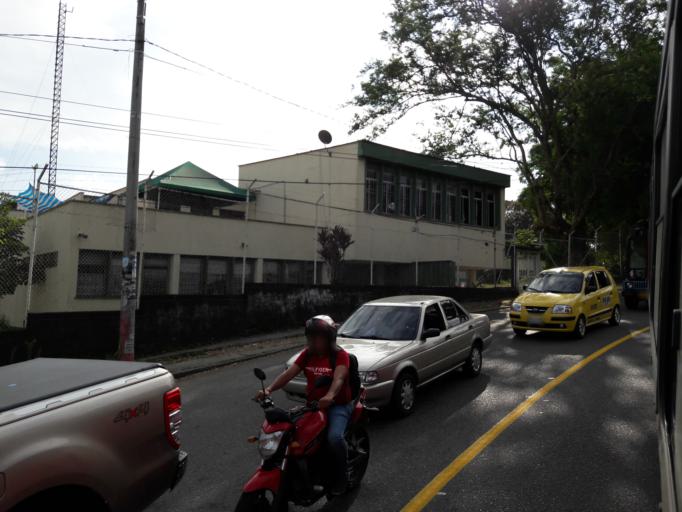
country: CO
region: Tolima
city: Ibague
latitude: 4.4358
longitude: -75.2103
